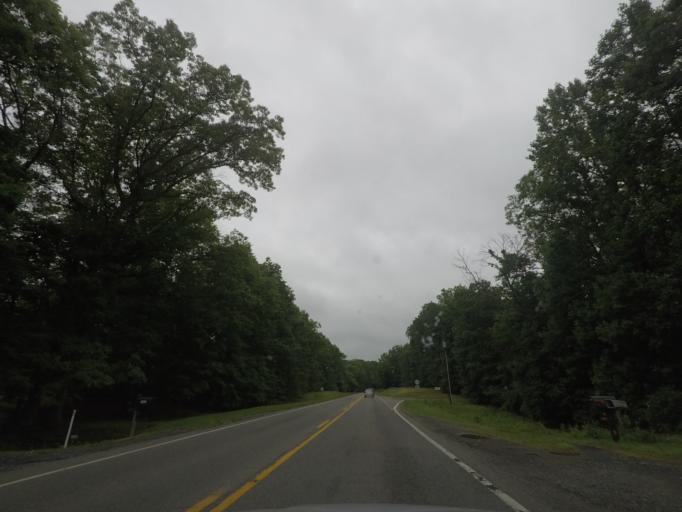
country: US
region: Virginia
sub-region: Fluvanna County
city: Palmyra
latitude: 37.8194
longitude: -78.2644
